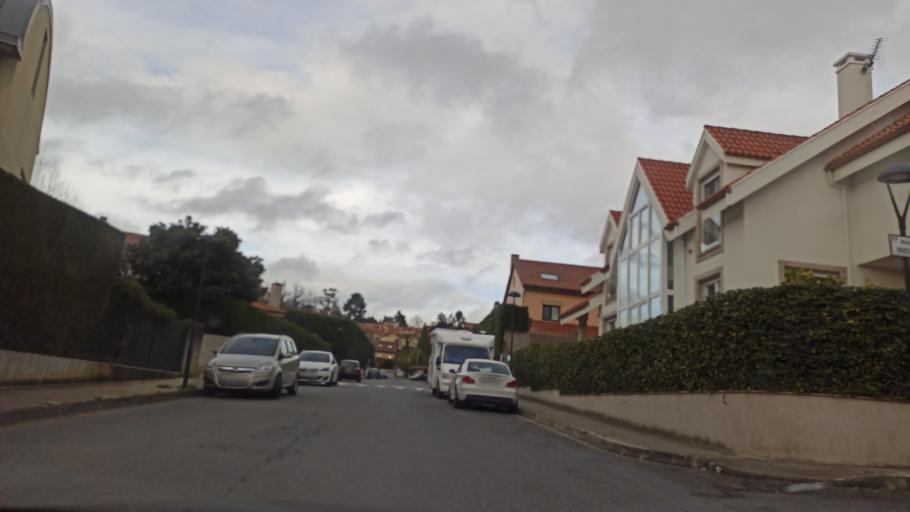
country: ES
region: Galicia
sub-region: Provincia da Coruna
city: Cambre
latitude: 43.3239
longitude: -8.3487
